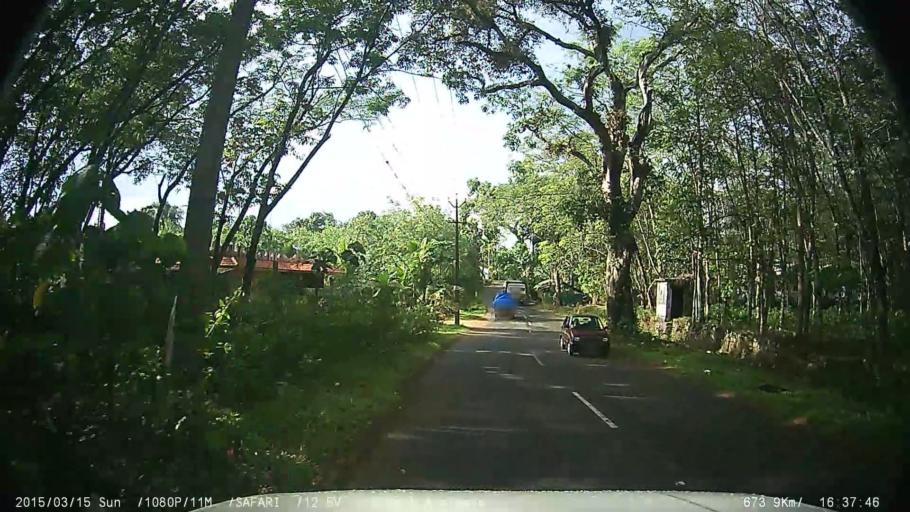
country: IN
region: Kerala
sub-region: Kottayam
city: Palackattumala
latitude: 9.8414
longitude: 76.6062
